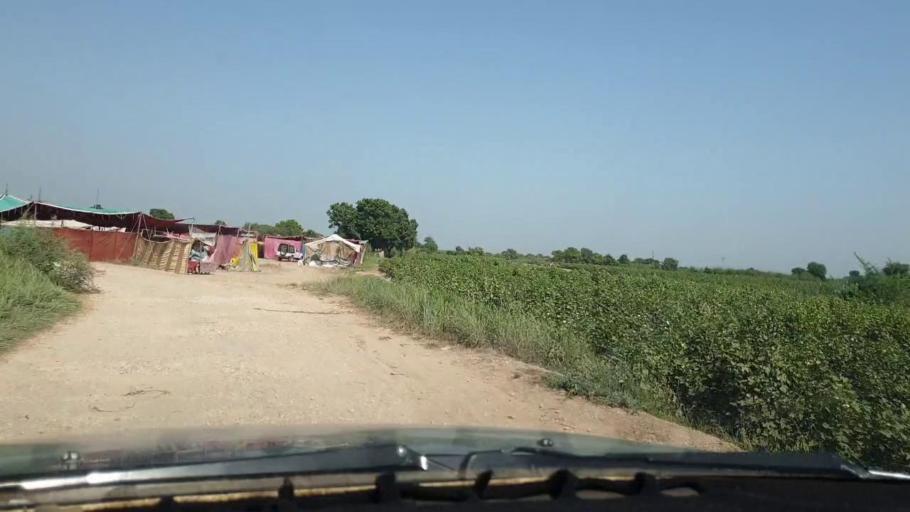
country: PK
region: Sindh
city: Chambar
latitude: 25.2307
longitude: 68.8687
